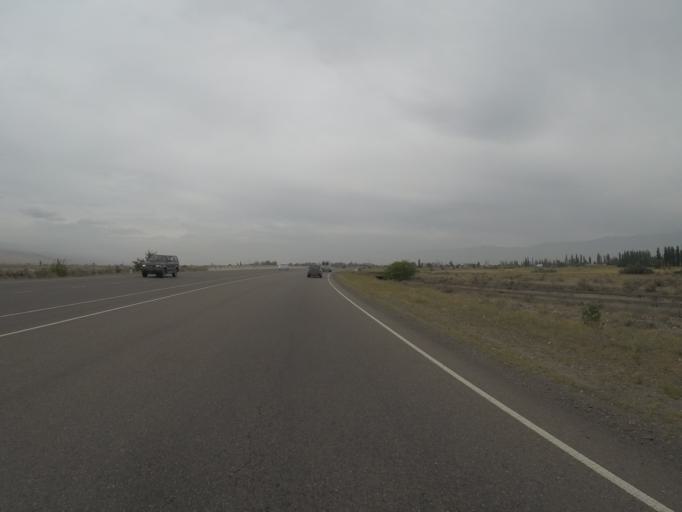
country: KG
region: Chuy
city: Bystrovka
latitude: 42.8282
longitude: 75.5383
